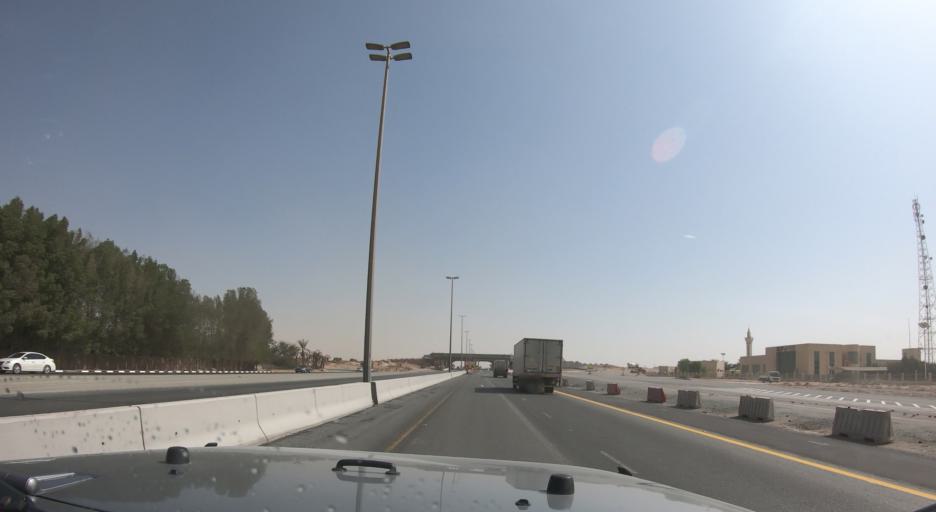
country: AE
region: Ash Shariqah
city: Sharjah
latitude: 25.2930
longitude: 55.6173
